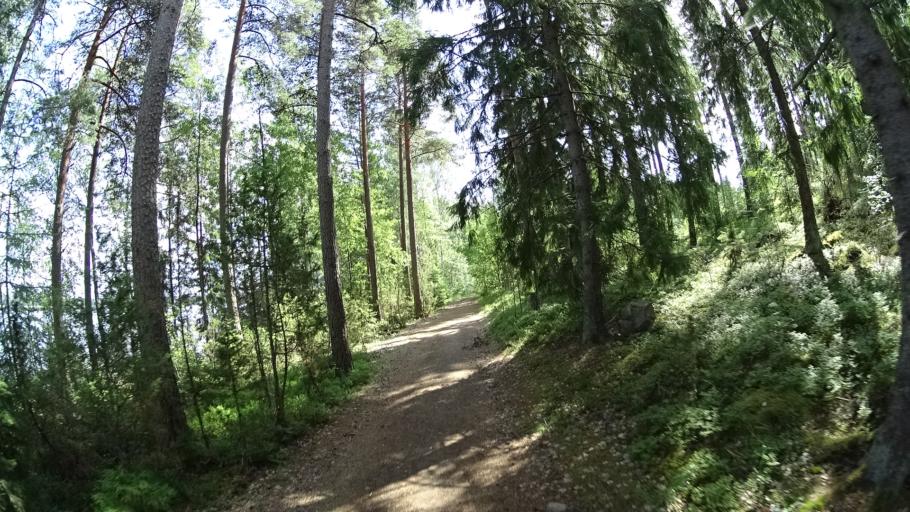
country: FI
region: Haeme
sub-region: Forssa
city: Tammela
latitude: 60.7764
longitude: 23.8544
